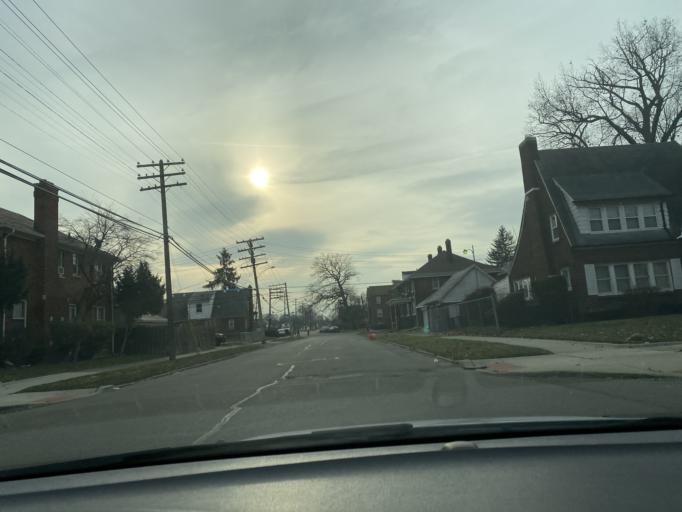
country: US
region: Michigan
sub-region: Wayne County
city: Highland Park
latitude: 42.3827
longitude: -83.1318
